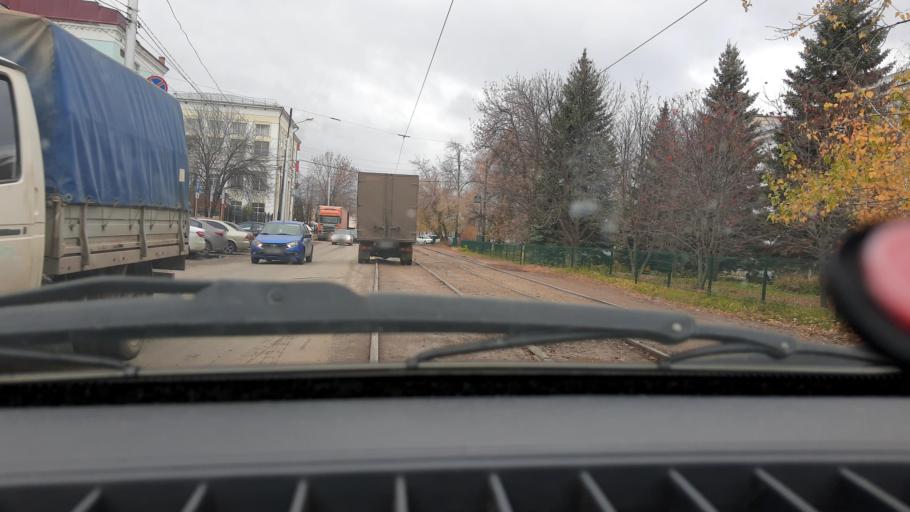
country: RU
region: Bashkortostan
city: Ufa
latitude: 54.7384
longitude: 55.9866
